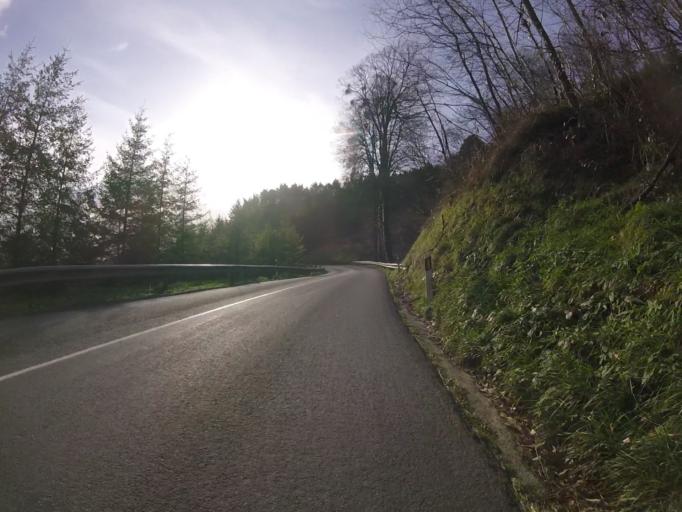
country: ES
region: Basque Country
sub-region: Provincia de Guipuzcoa
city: Asteasu
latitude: 43.2045
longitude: -2.1171
